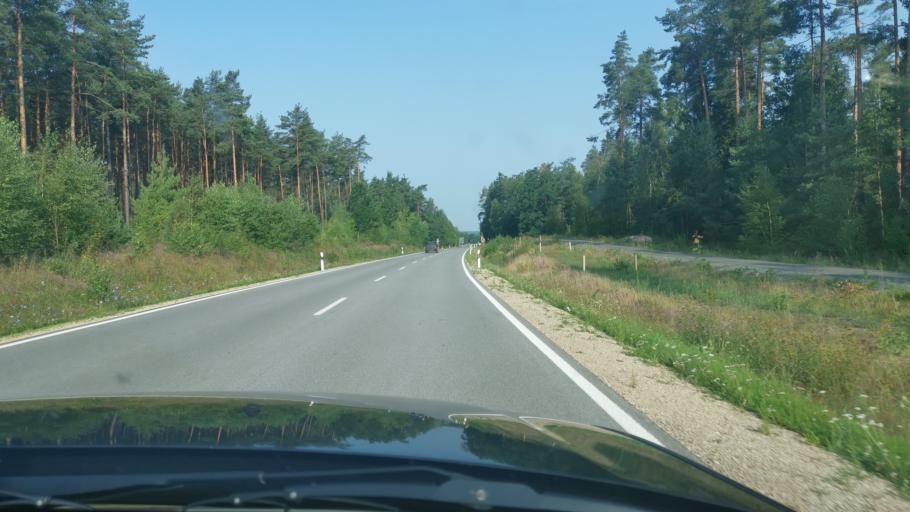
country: DE
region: Bavaria
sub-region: Upper Palatinate
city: Schnaittenbach
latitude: 49.5413
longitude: 12.0655
